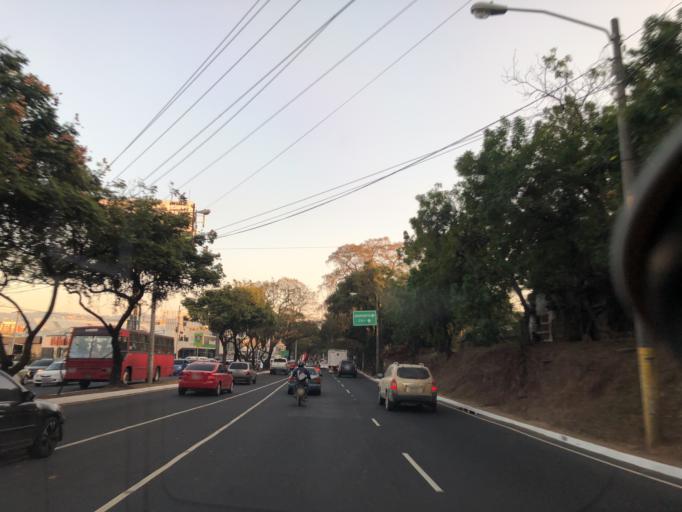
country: GT
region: Guatemala
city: Guatemala City
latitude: 14.6016
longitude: -90.5267
